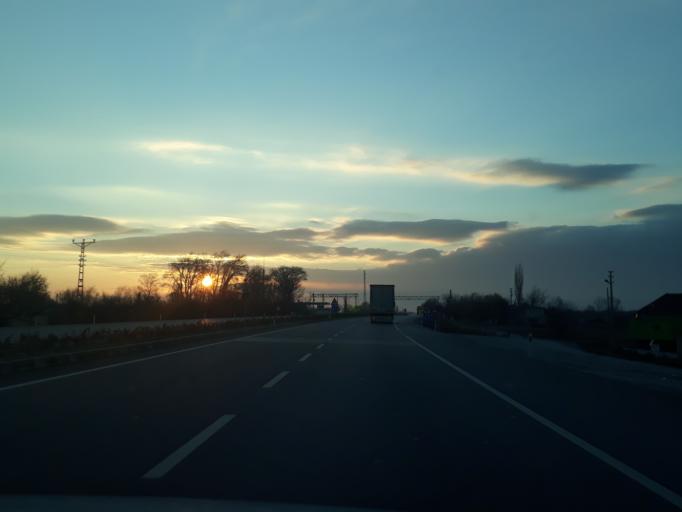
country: TR
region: Konya
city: Yarma
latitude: 37.8093
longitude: 32.8747
